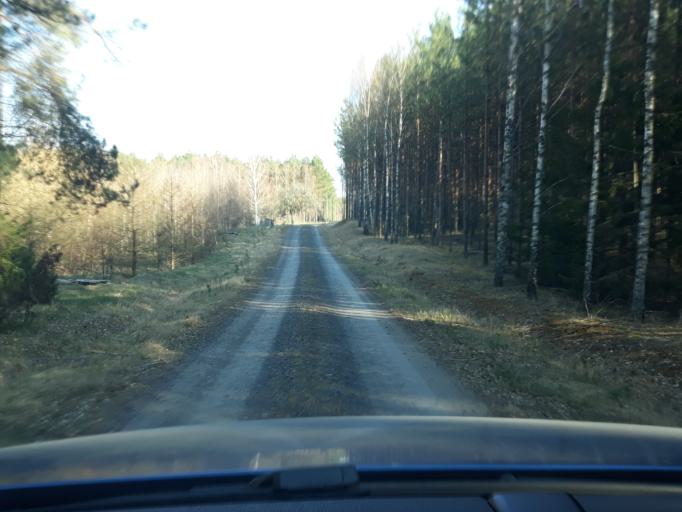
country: PL
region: Pomeranian Voivodeship
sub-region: Powiat bytowski
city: Lipnica
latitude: 53.9127
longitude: 17.4951
